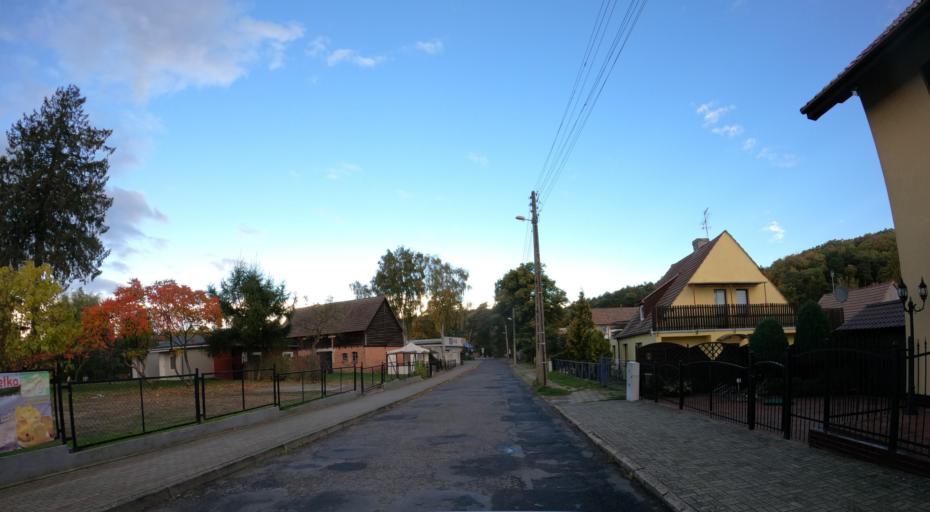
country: PL
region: West Pomeranian Voivodeship
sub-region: Powiat kamienski
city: Miedzyzdroje
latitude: 53.9658
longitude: 14.5722
